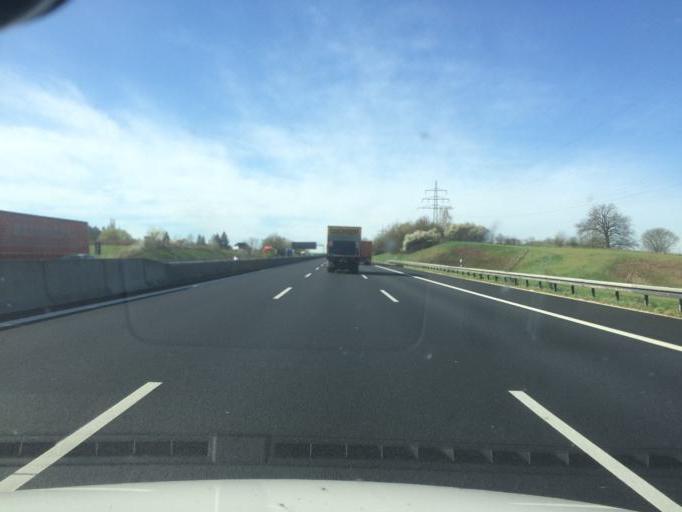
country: DE
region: Bavaria
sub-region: Regierungsbezirk Mittelfranken
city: Lauf an der Pegnitz
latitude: 49.4946
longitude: 11.2805
